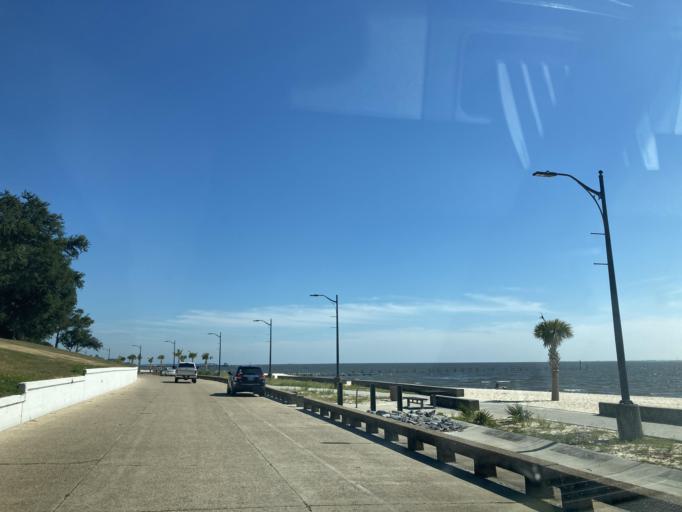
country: US
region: Mississippi
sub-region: Jackson County
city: Ocean Springs
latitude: 30.4090
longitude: -88.8376
